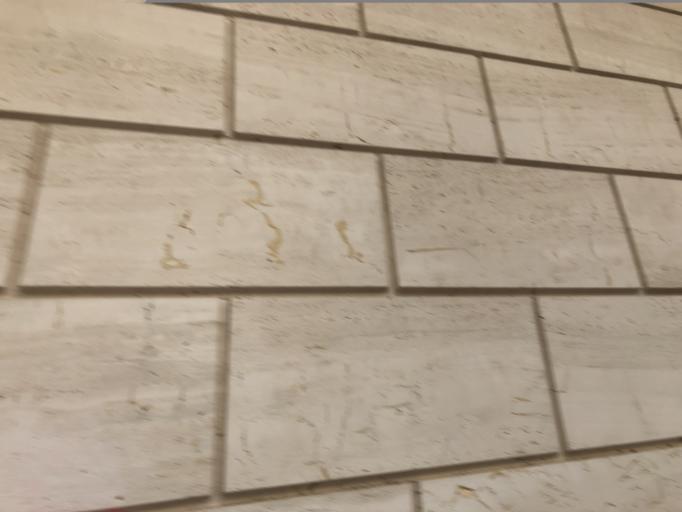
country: IT
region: Apulia
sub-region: Provincia di Barletta - Andria - Trani
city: Andria
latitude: 41.2261
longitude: 16.3077
